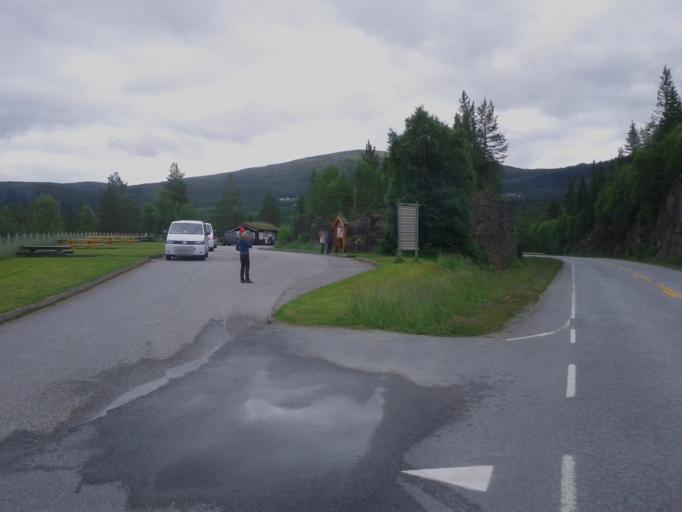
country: NO
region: Sor-Trondelag
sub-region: Holtalen
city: Alen
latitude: 62.8596
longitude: 11.2124
